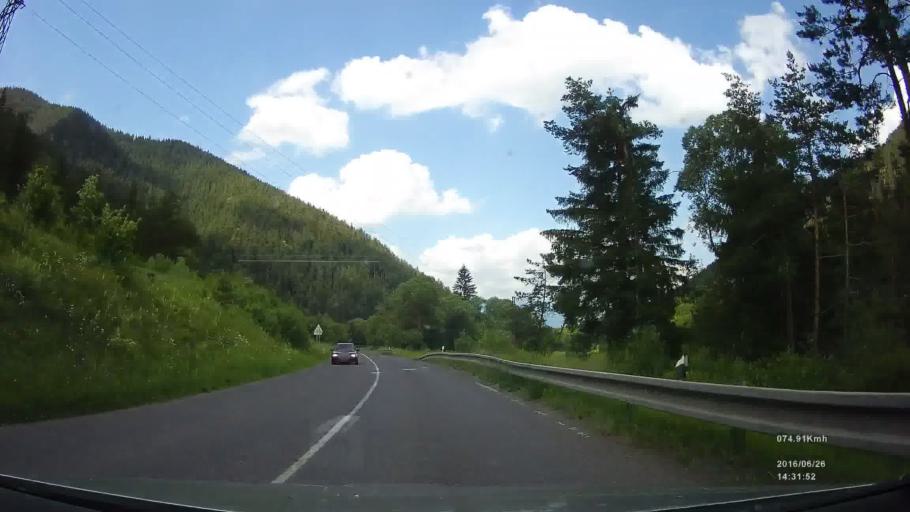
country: SK
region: Zilinsky
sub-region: Okres Zilina
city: Liptovsky Hradok
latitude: 49.0060
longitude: 19.7666
